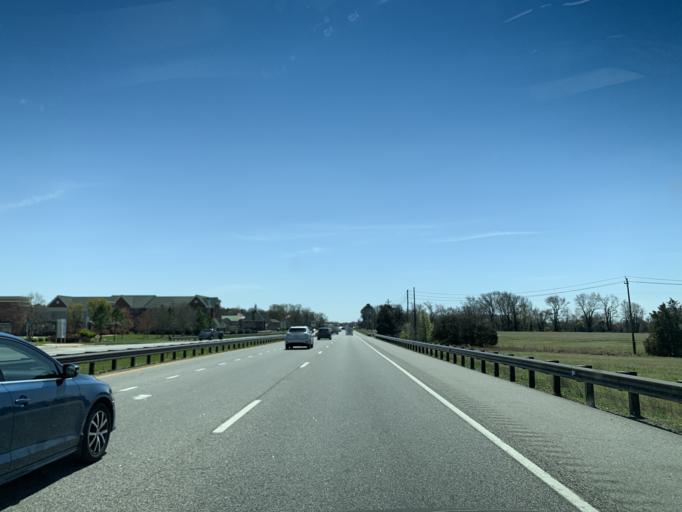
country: US
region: Maryland
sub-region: Talbot County
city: Easton
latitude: 38.7903
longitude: -76.0603
